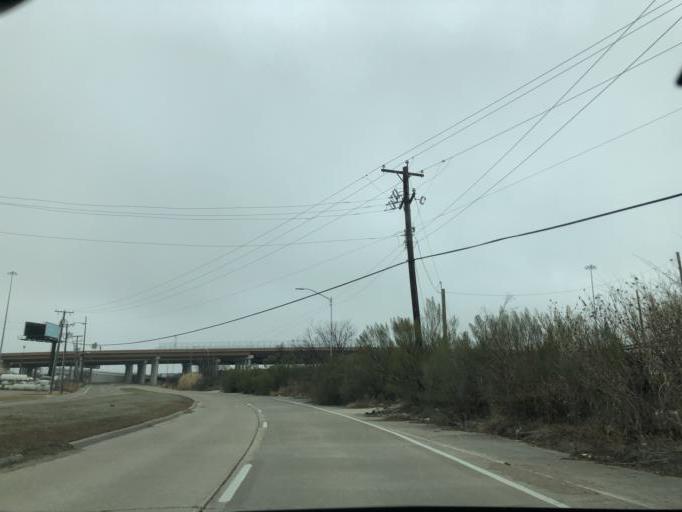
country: US
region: Texas
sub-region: Tarrant County
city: Haltom City
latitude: 32.8107
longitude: -97.3117
